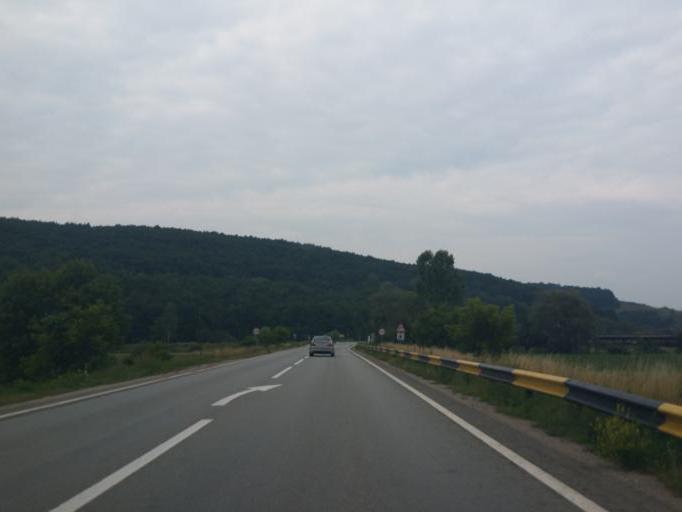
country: RO
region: Salaj
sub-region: Comuna Zimbor
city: Zimbor
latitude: 46.9925
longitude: 23.2507
